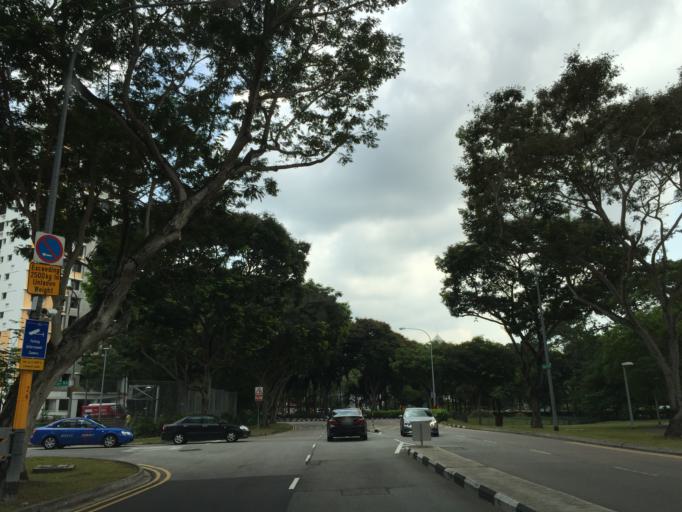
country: SG
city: Singapore
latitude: 1.3167
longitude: 103.8503
